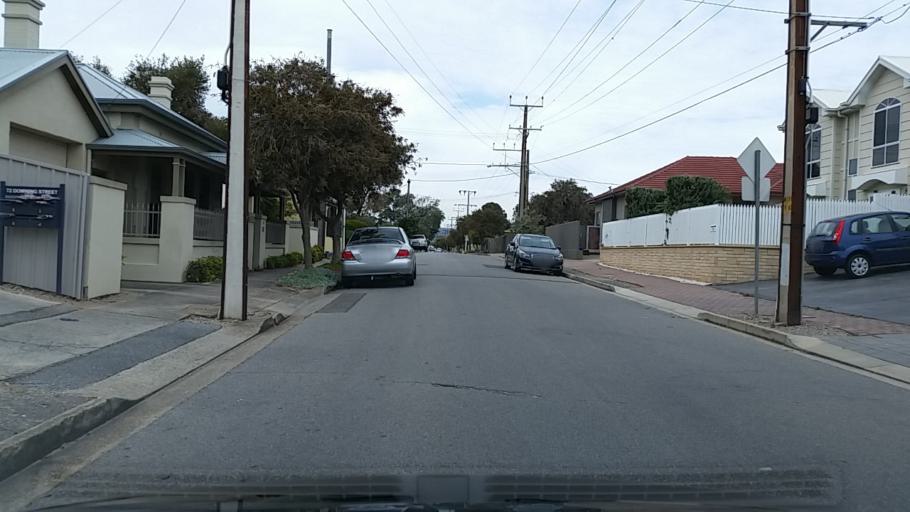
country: AU
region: South Australia
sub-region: Holdfast Bay
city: North Brighton
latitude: -35.0091
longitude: 138.5140
